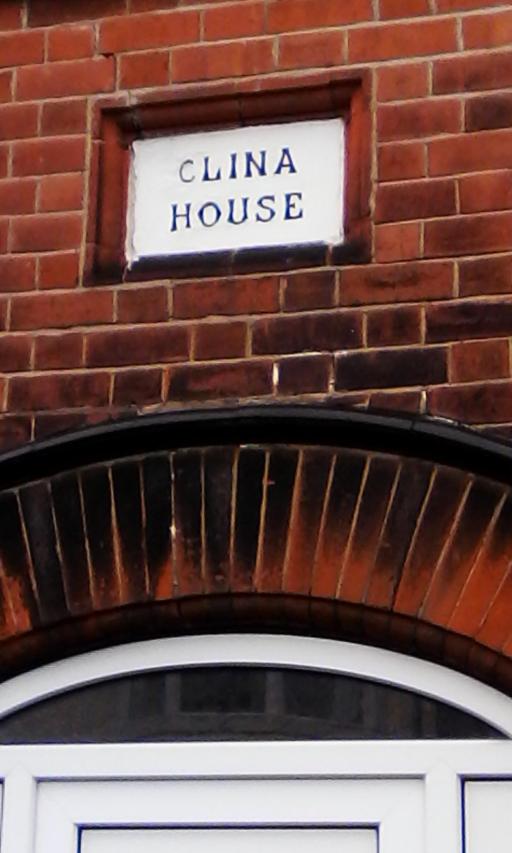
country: GB
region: England
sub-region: Nottinghamshire
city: Arnold
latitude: 52.9724
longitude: -1.1180
